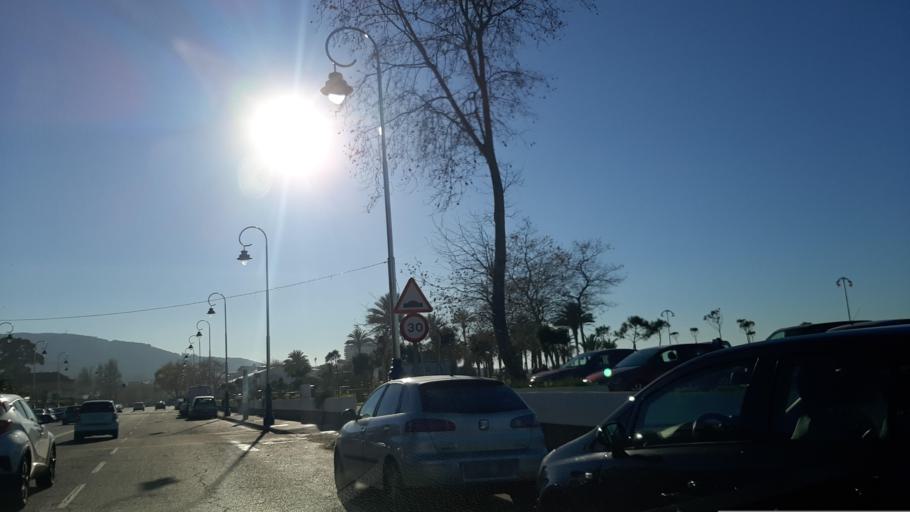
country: ES
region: Galicia
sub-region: Provincia de Pontevedra
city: Cangas
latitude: 42.2080
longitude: -8.7758
